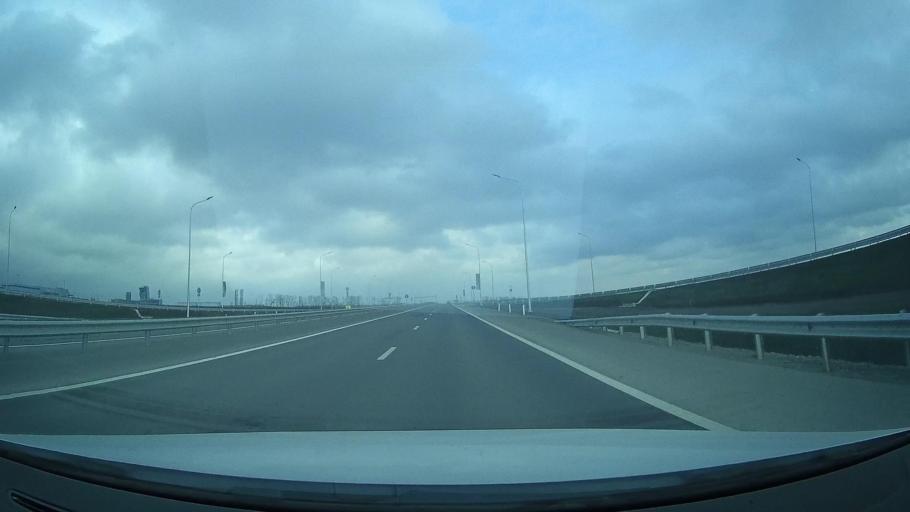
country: RU
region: Rostov
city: Grushevskaya
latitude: 47.4869
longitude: 39.9370
